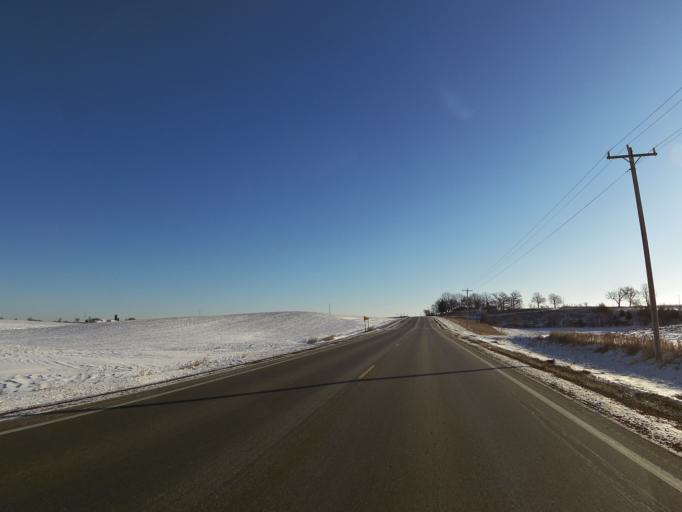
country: US
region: Minnesota
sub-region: Carver County
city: Carver
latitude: 44.7327
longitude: -93.5666
